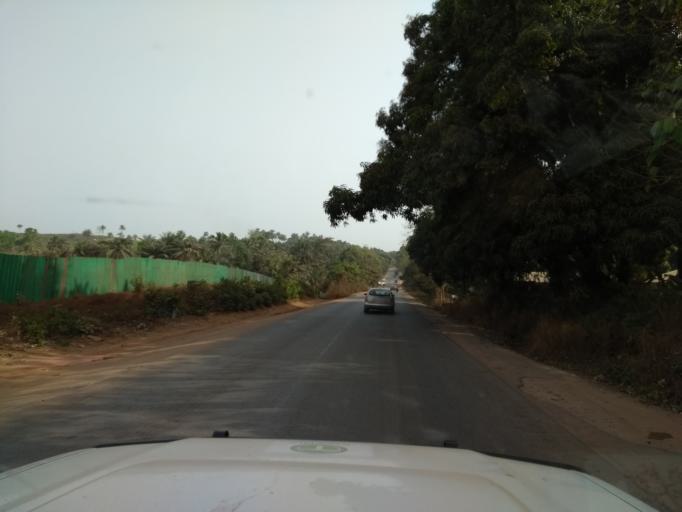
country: GN
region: Kindia
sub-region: Prefecture de Dubreka
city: Dubreka
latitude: 9.8411
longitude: -13.4879
